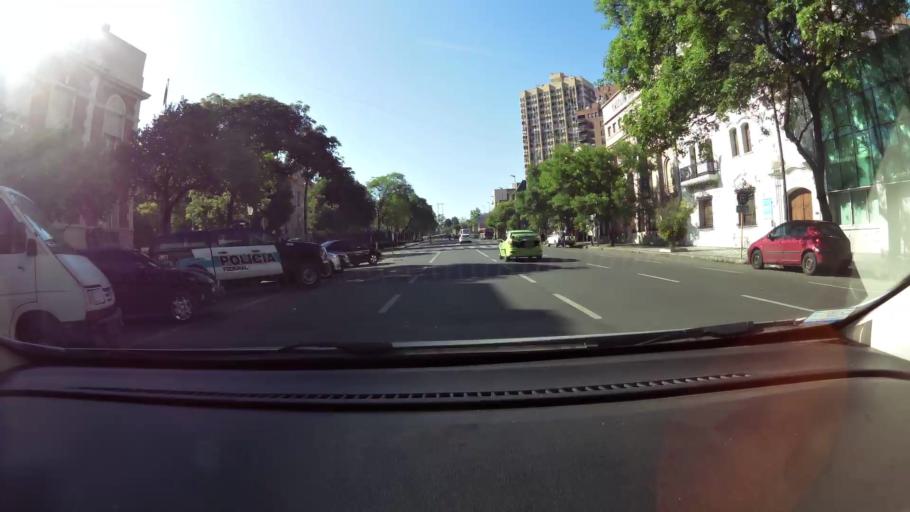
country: AR
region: Cordoba
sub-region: Departamento de Capital
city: Cordoba
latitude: -31.4264
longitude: -64.1859
